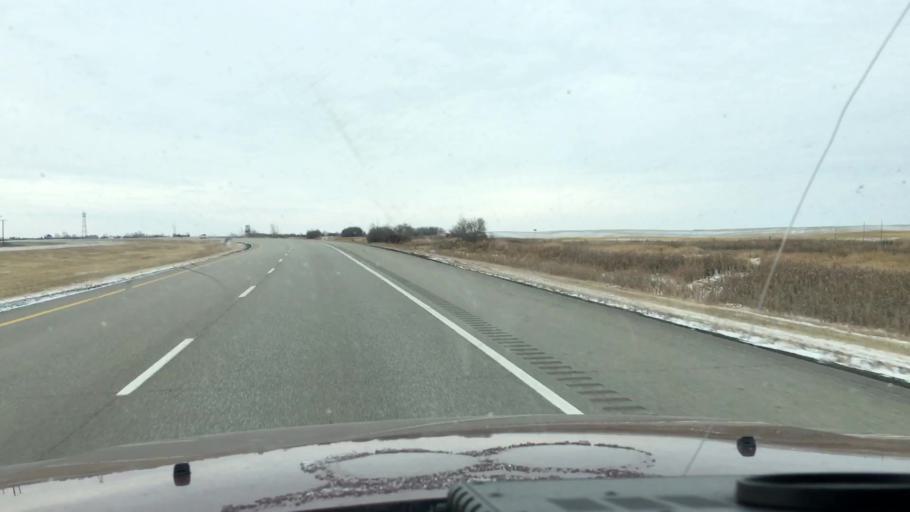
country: CA
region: Saskatchewan
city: Watrous
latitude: 51.3821
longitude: -106.1604
